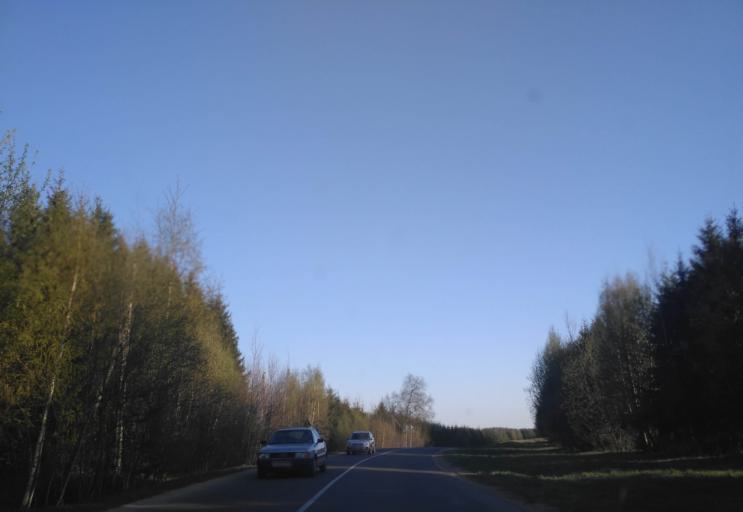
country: BY
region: Minsk
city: Radashkovichy
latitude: 54.1288
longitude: 27.2004
